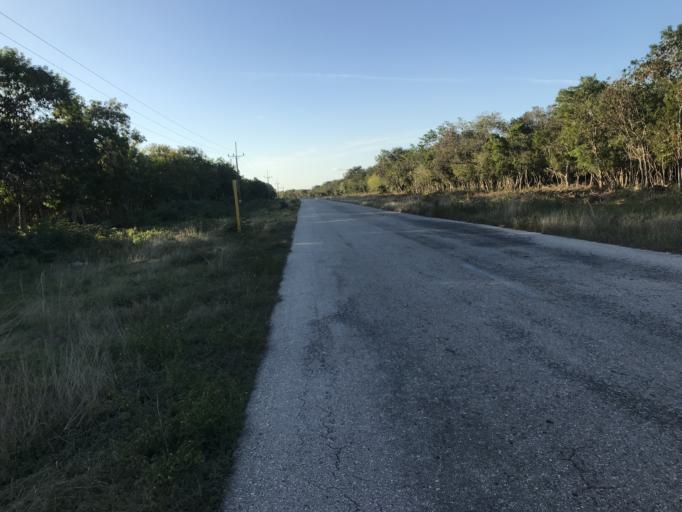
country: CU
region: Cienfuegos
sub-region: Municipio de Aguada de Pasajeros
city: Aguada de Pasajeros
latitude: 22.0740
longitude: -81.0583
